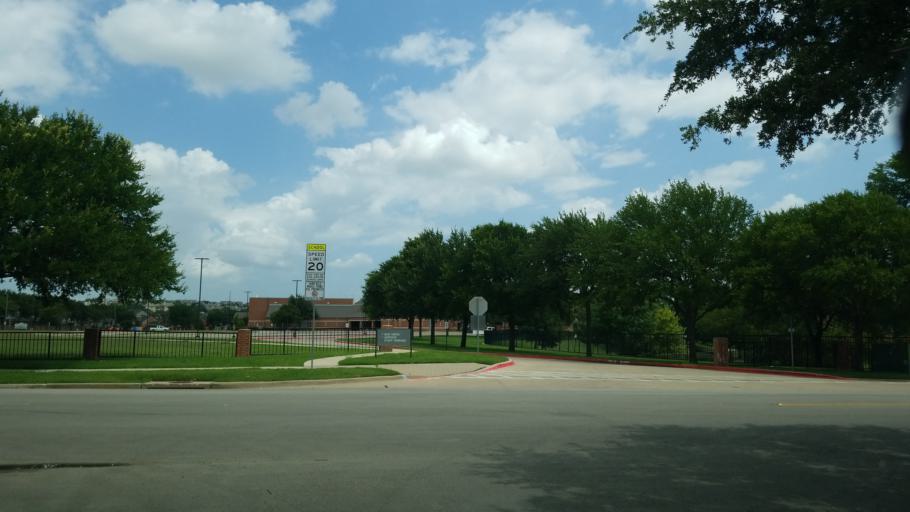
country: US
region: Texas
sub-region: Dallas County
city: Farmers Branch
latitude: 32.9358
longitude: -96.9560
